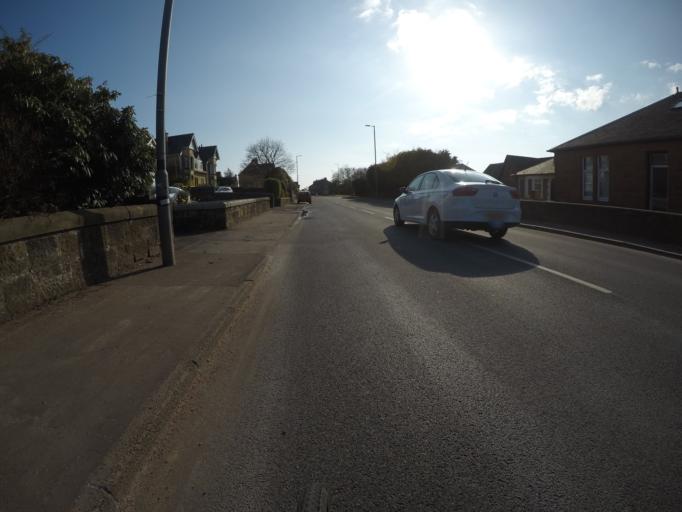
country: GB
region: Scotland
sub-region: North Ayrshire
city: Kilwinning
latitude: 55.6542
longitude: -4.7130
